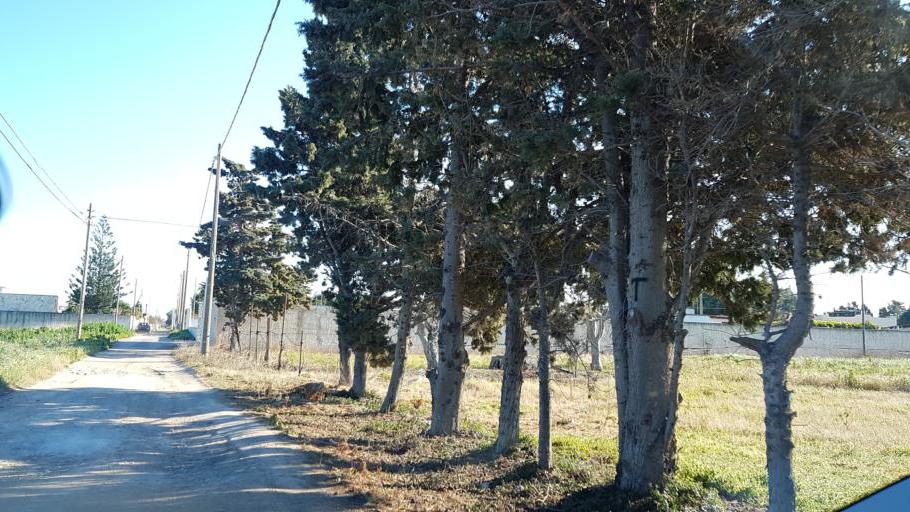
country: IT
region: Apulia
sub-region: Provincia di Brindisi
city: Materdomini
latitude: 40.6729
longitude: 17.9423
